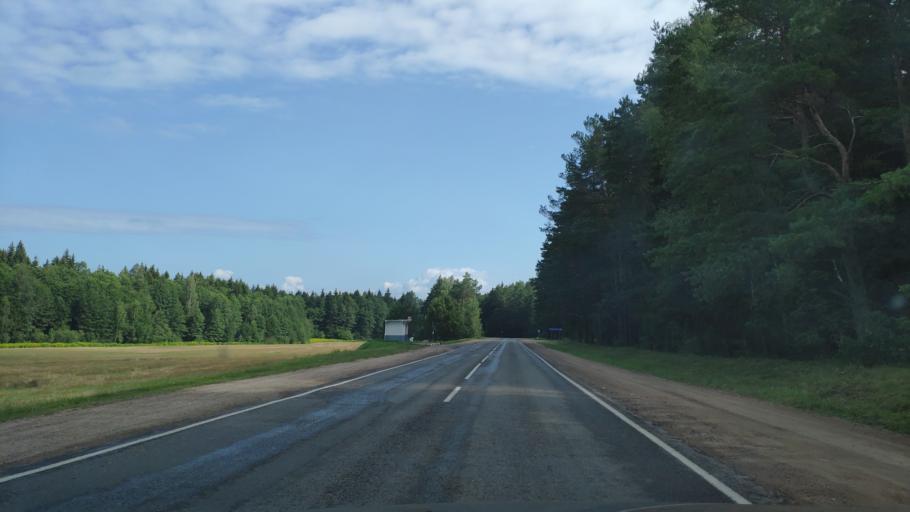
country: BY
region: Minsk
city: Zaslawye
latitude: 53.9694
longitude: 27.2468
